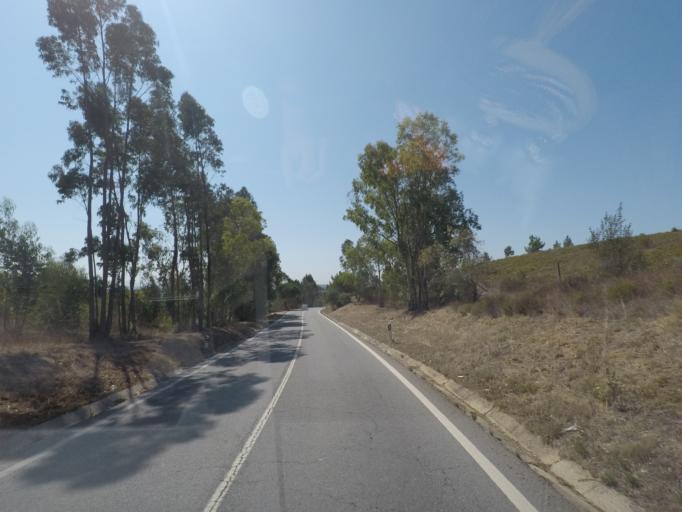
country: PT
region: Beja
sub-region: Odemira
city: Sao Teotonio
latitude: 37.5297
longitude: -8.6992
